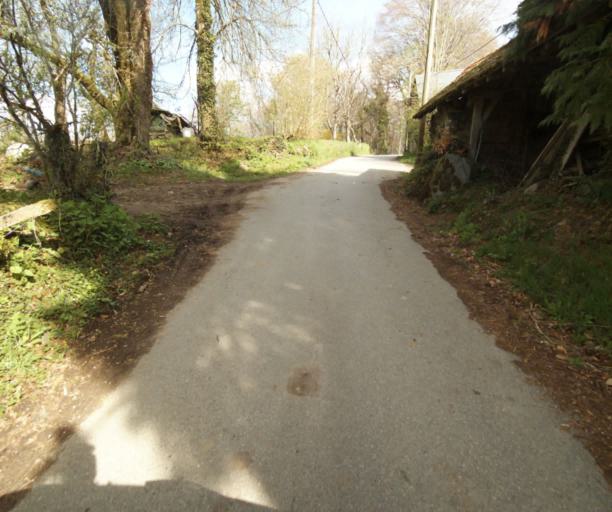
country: FR
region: Limousin
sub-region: Departement de la Correze
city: Correze
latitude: 45.3487
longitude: 1.8583
